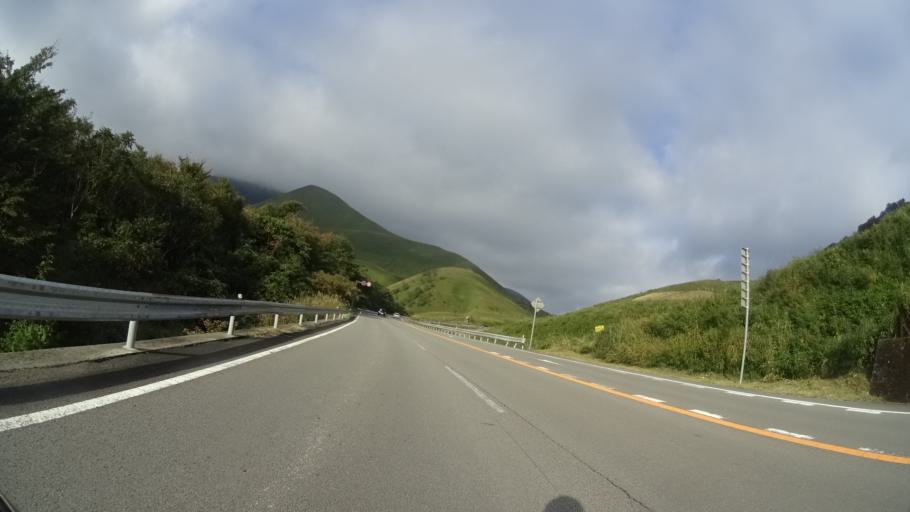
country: JP
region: Oita
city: Beppu
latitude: 33.2601
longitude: 131.3834
